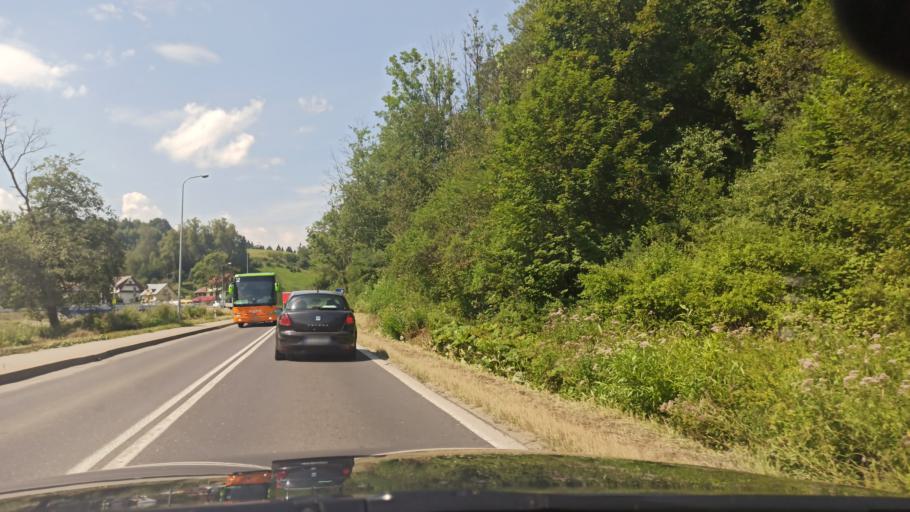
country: PL
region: Lesser Poland Voivodeship
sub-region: Powiat nowotarski
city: Kroscienko nad Dunajcem
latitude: 49.4393
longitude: 20.4012
